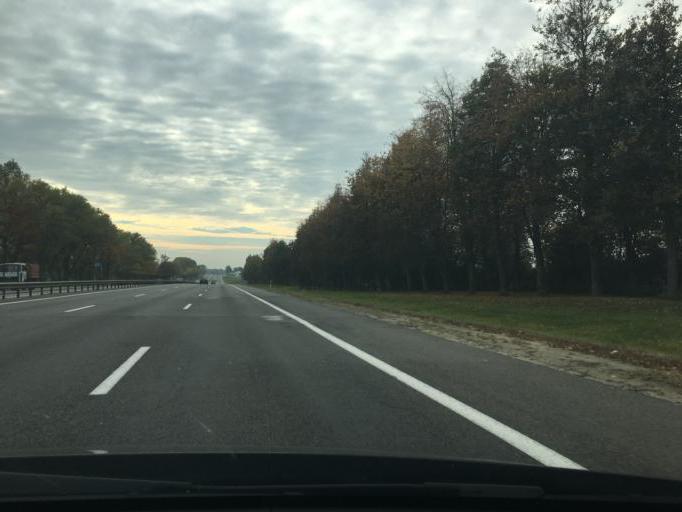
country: BY
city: Fanipol
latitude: 53.7489
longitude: 27.3217
